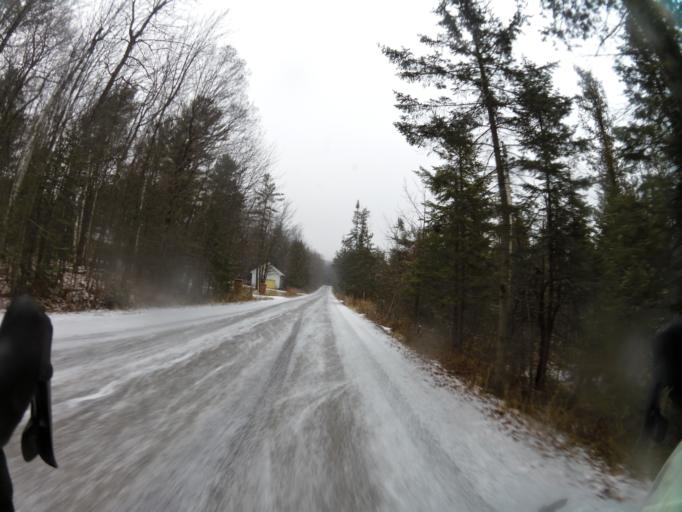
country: CA
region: Quebec
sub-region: Outaouais
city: Gatineau
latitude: 45.4882
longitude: -75.8406
